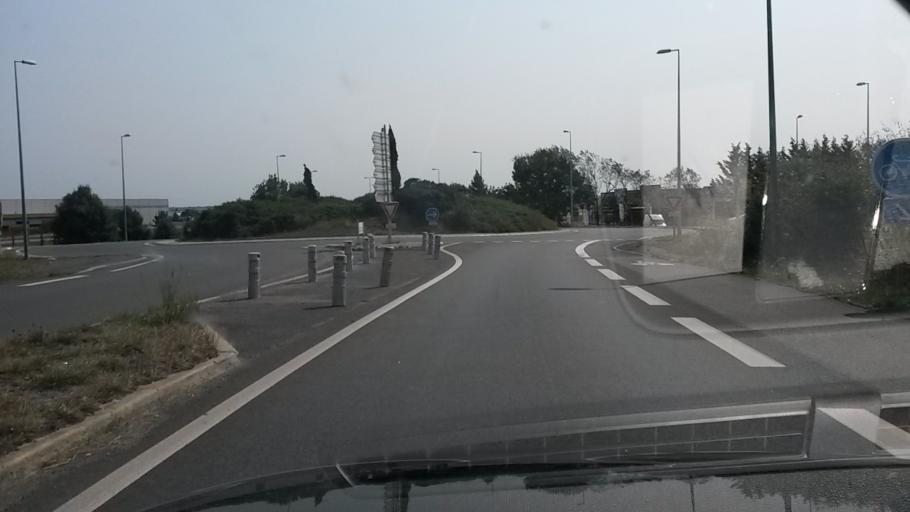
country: FR
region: Pays de la Loire
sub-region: Departement de la Loire-Atlantique
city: Saint-Gereon
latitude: 47.4001
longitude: -1.1903
